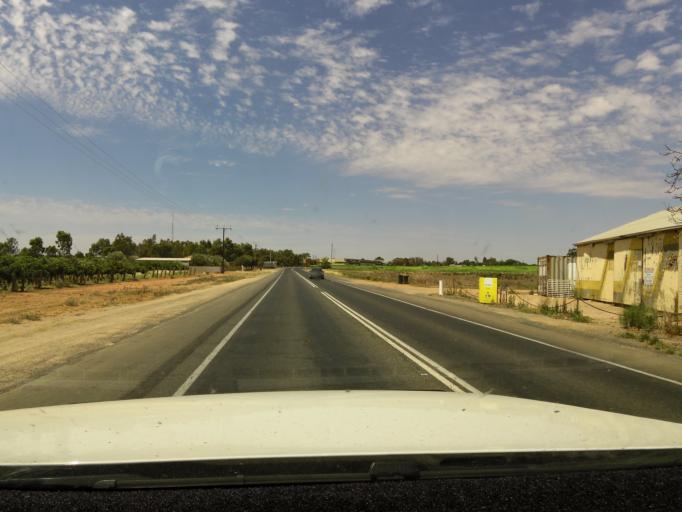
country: AU
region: South Australia
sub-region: Berri and Barmera
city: Berri
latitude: -34.2809
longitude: 140.5668
